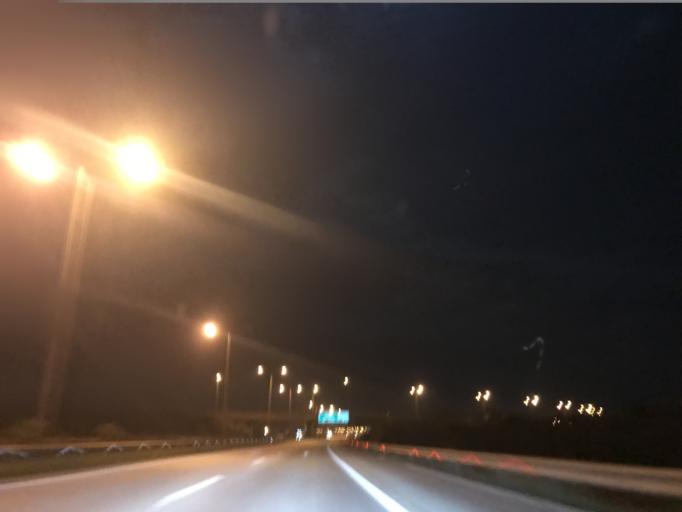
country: TR
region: Hatay
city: Mahmutlar
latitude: 36.9645
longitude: 36.1104
